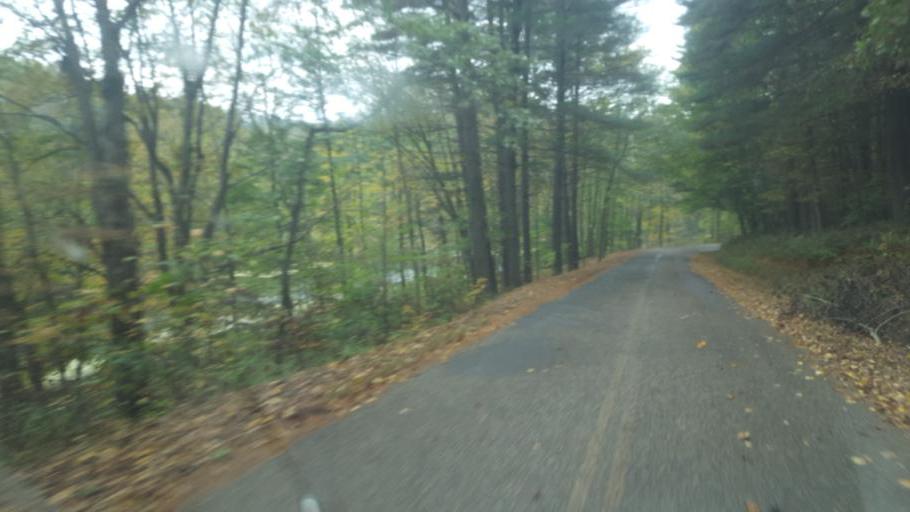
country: US
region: Ohio
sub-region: Carroll County
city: Carrollton
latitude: 40.4600
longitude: -81.1373
